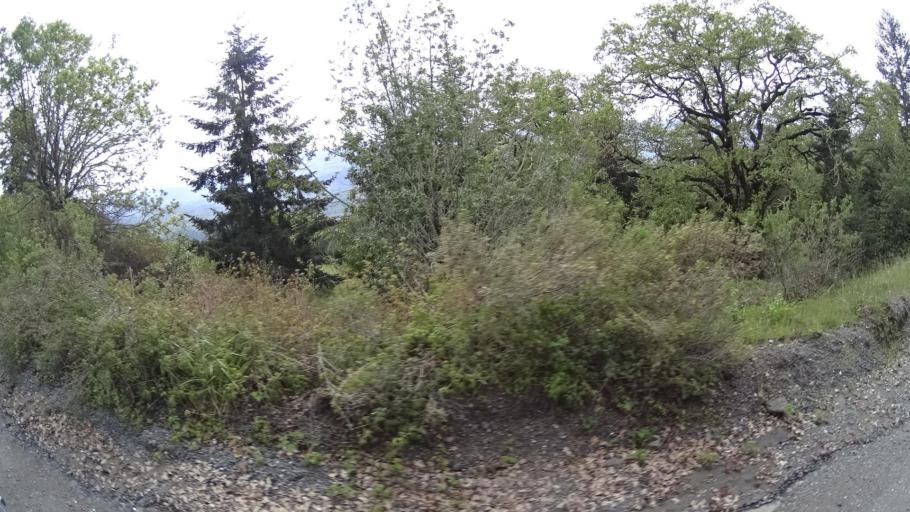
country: US
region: California
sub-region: Humboldt County
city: Blue Lake
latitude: 40.8586
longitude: -123.9116
